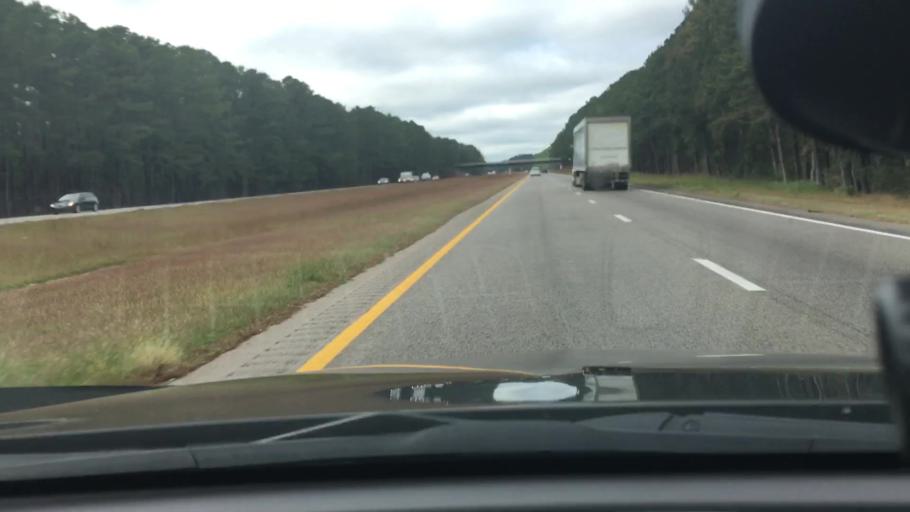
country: US
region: North Carolina
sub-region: Wilson County
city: Lucama
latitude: 35.7804
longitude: -78.0816
